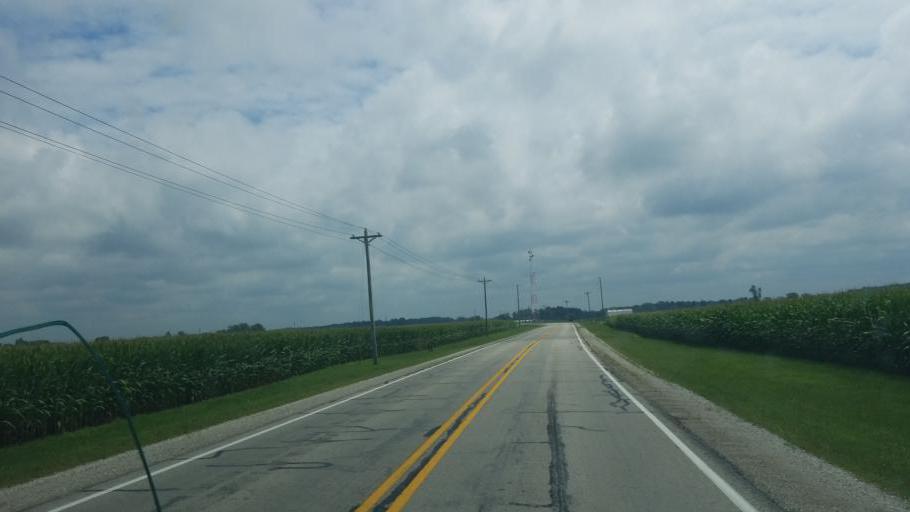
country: US
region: Indiana
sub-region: Huntington County
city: Warren
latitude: 40.6685
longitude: -85.4470
